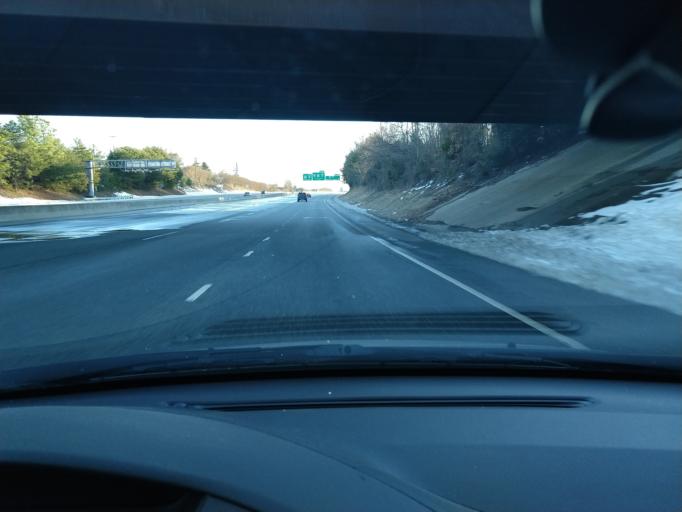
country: US
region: North Carolina
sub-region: Guilford County
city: Greensboro
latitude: 36.0407
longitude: -79.8180
